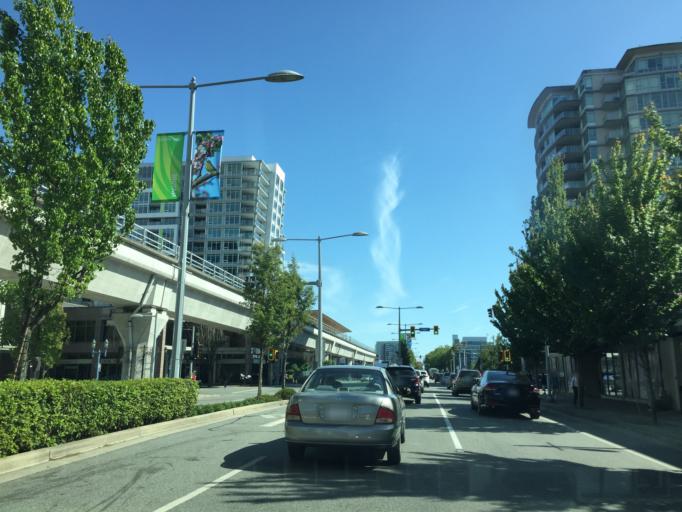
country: CA
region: British Columbia
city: Richmond
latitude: 49.1696
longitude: -123.1366
